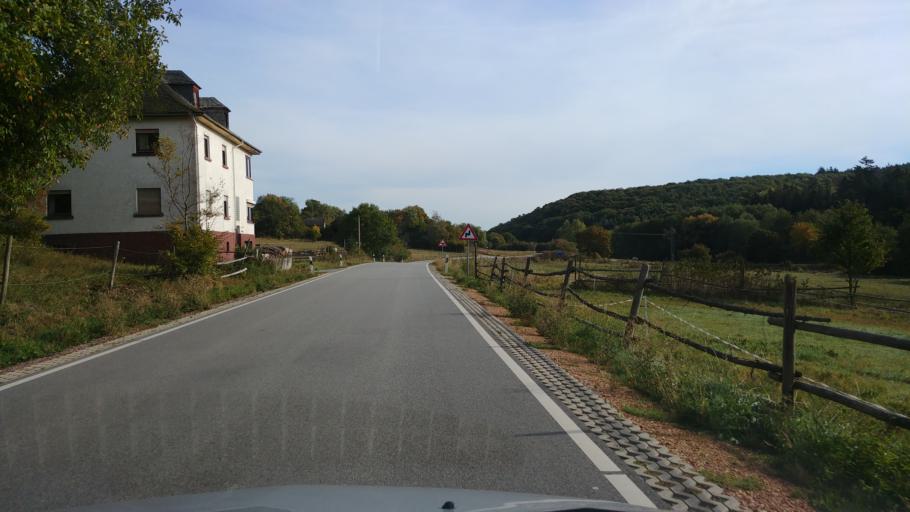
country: DE
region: Rheinland-Pfalz
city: Reckenroth
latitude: 50.2188
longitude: 8.0047
